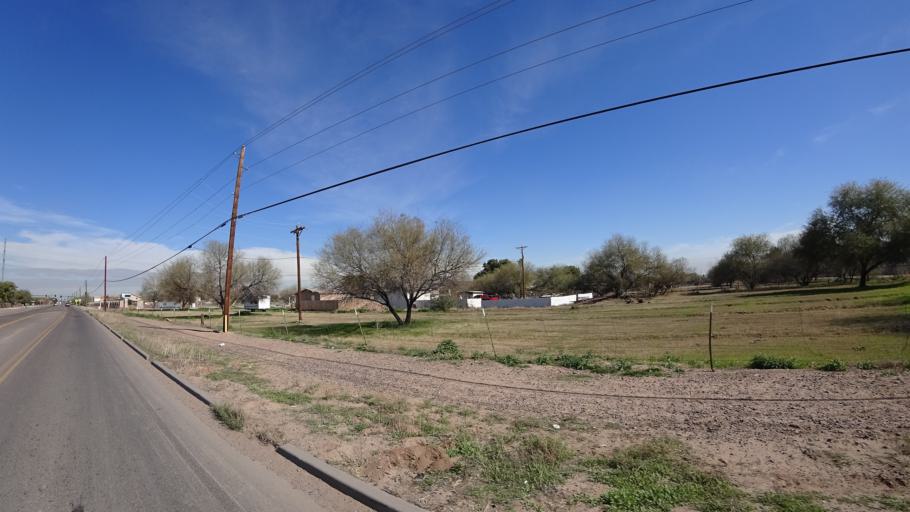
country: US
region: Arizona
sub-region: Maricopa County
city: Laveen
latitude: 33.4132
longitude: -112.2041
